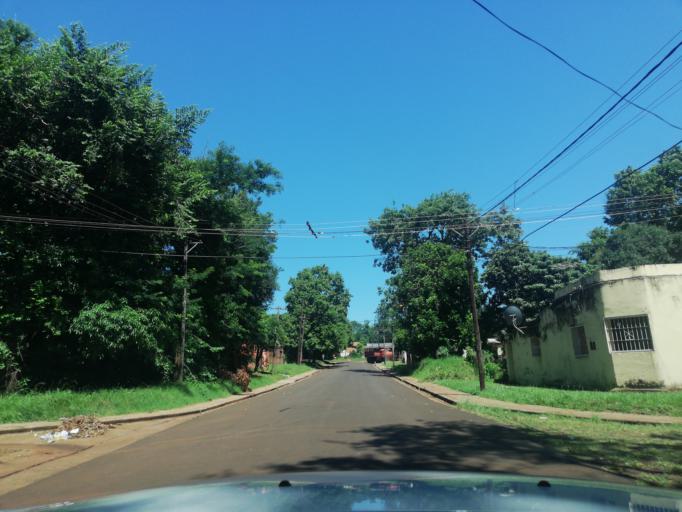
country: AR
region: Misiones
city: Garupa
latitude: -27.4812
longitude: -55.8306
